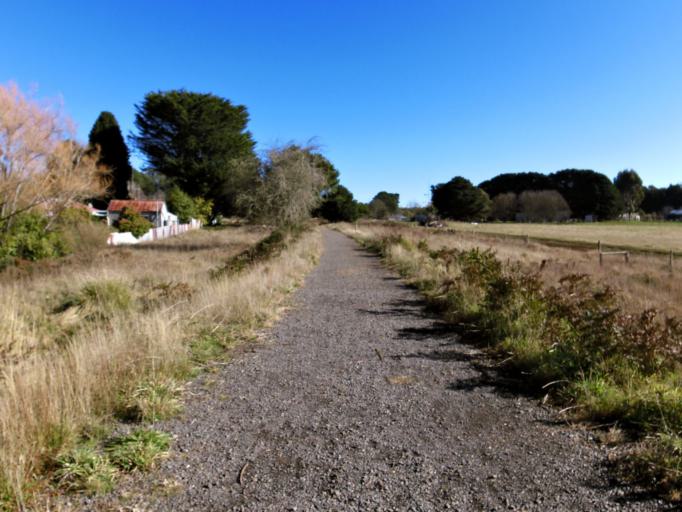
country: AU
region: Victoria
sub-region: Moorabool
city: Bacchus Marsh
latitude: -37.3852
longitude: 144.3194
